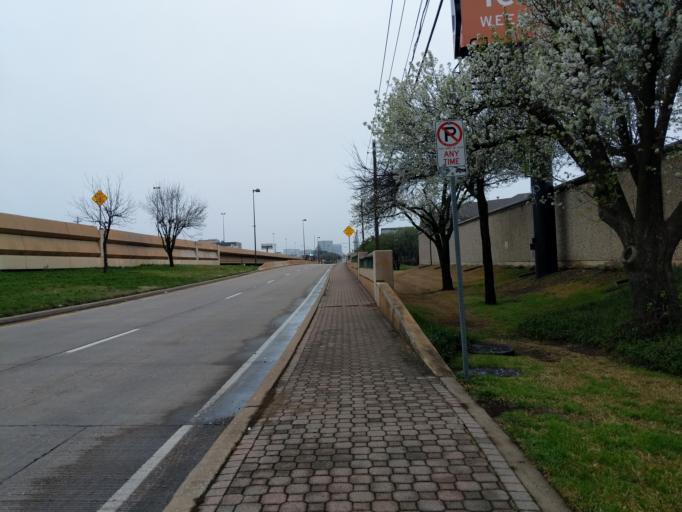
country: US
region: Texas
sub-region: Dallas County
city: Richardson
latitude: 32.9065
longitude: -96.7694
